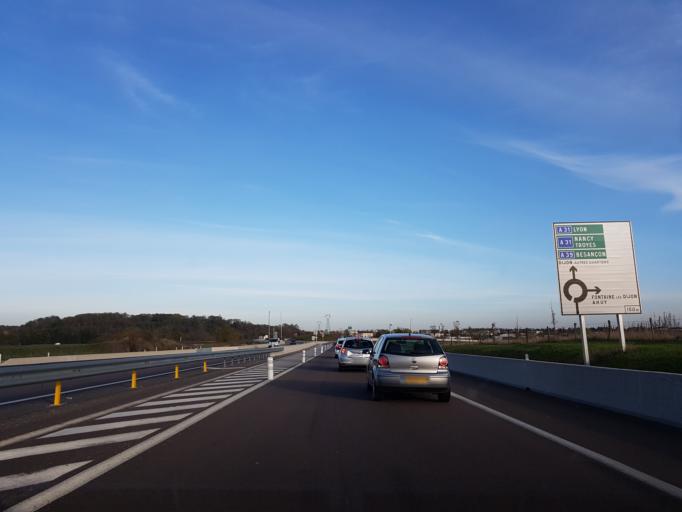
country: FR
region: Bourgogne
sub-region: Departement de la Cote-d'Or
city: Ahuy
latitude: 47.3583
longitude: 5.0290
